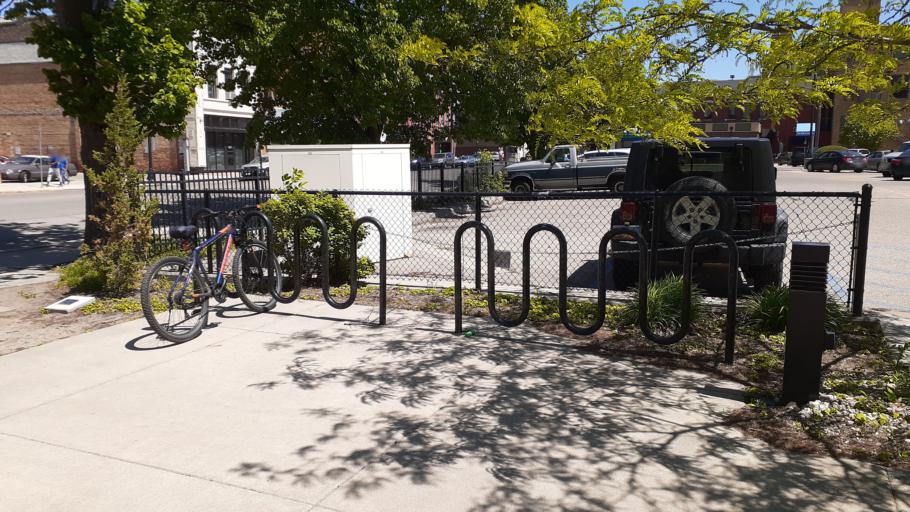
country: US
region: North Dakota
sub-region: Cass County
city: Fargo
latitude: 46.8758
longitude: -96.7900
